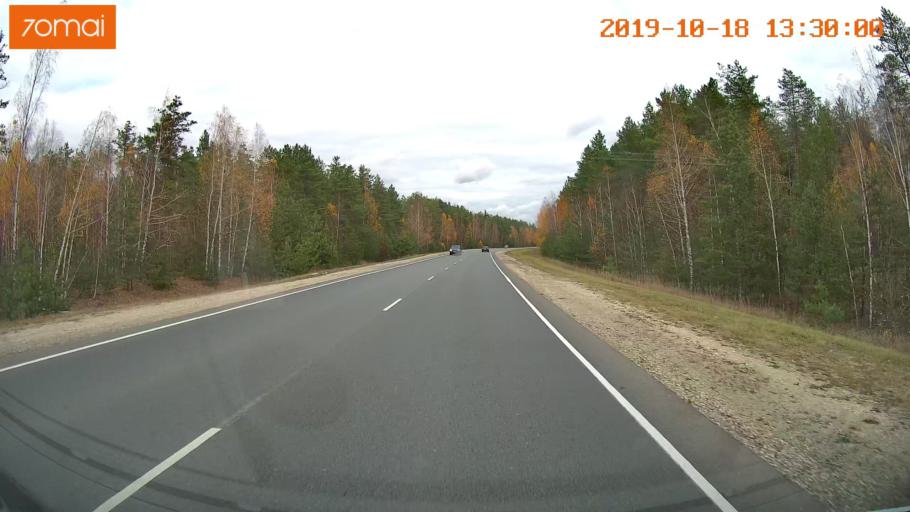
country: RU
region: Rjazan
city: Solotcha
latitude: 54.8036
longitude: 39.8793
